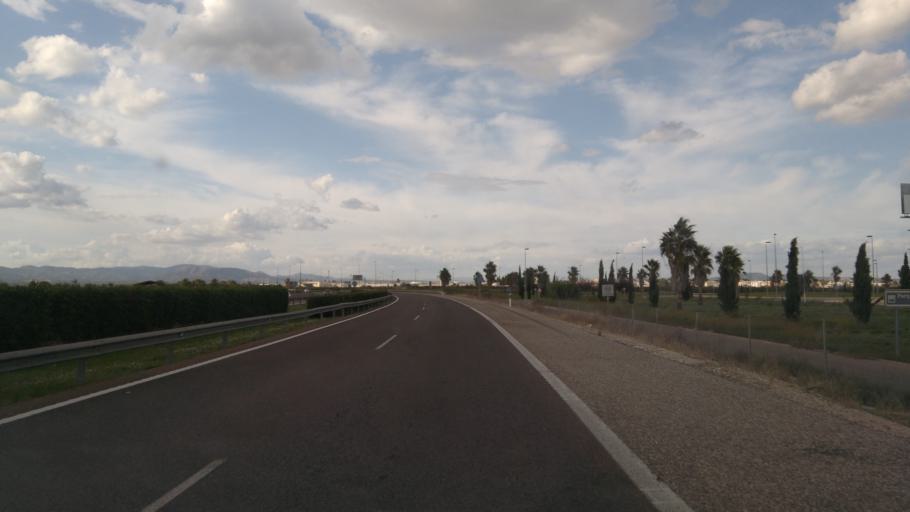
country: ES
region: Valencia
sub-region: Provincia de Valencia
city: Guadassuar
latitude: 39.1737
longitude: -0.4670
